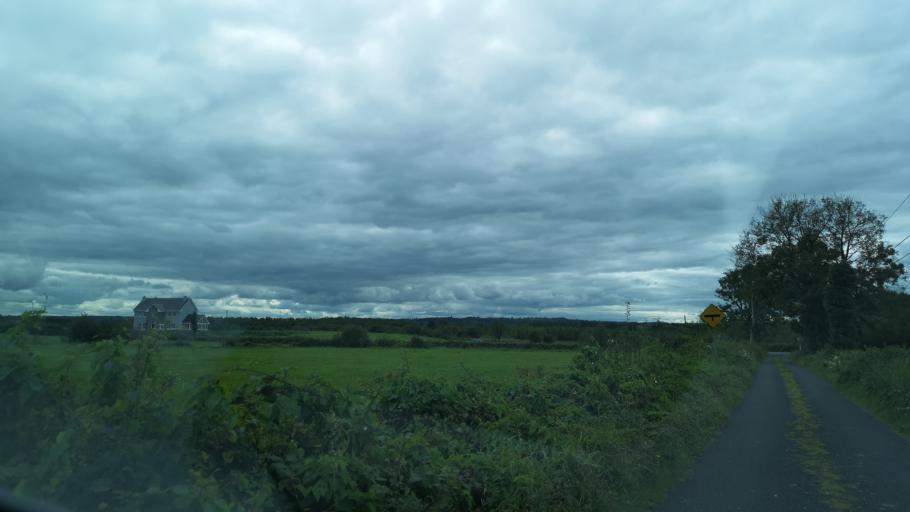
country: IE
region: Connaught
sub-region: County Galway
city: Loughrea
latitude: 53.1550
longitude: -8.4361
